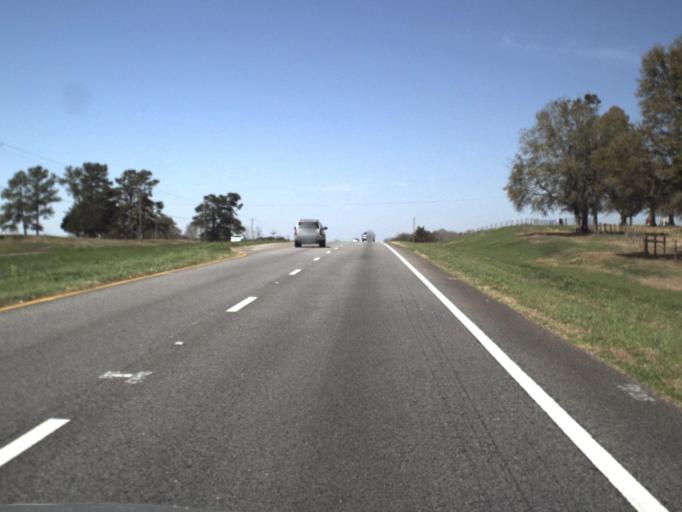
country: US
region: Florida
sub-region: Jackson County
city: Graceville
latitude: 30.9075
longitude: -85.3767
